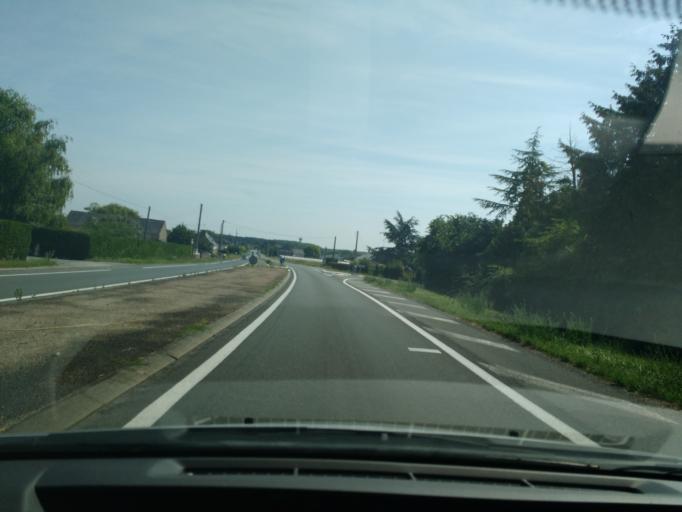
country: FR
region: Pays de la Loire
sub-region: Departement de Maine-et-Loire
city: Corne
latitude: 47.4741
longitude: -0.3360
